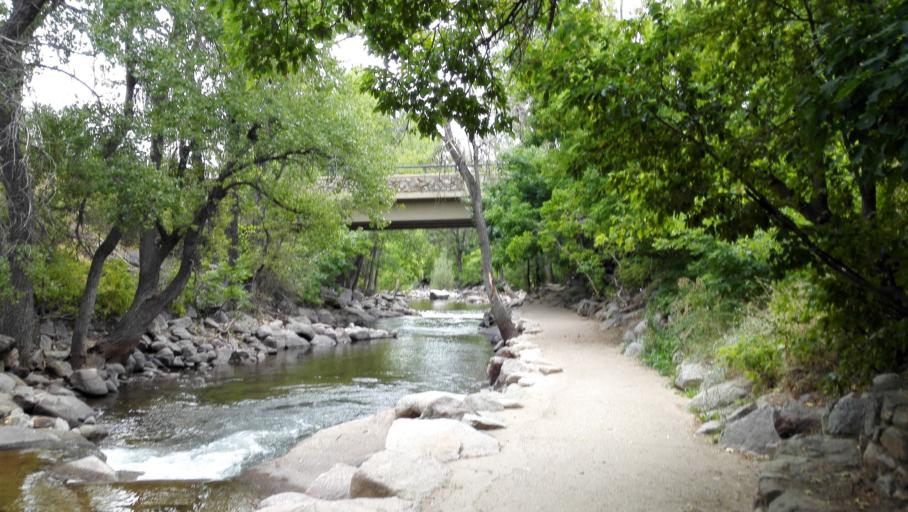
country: US
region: Colorado
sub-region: Boulder County
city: Boulder
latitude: 40.0132
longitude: -105.2984
